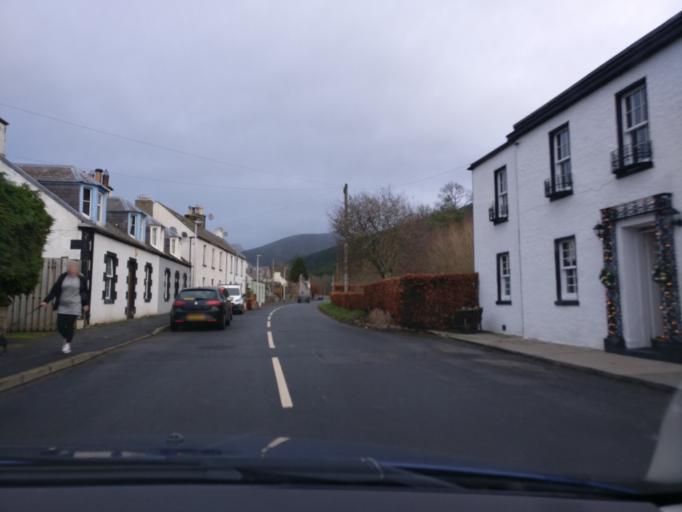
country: GB
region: Scotland
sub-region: The Scottish Borders
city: Innerleithen
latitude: 55.6235
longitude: -3.0609
